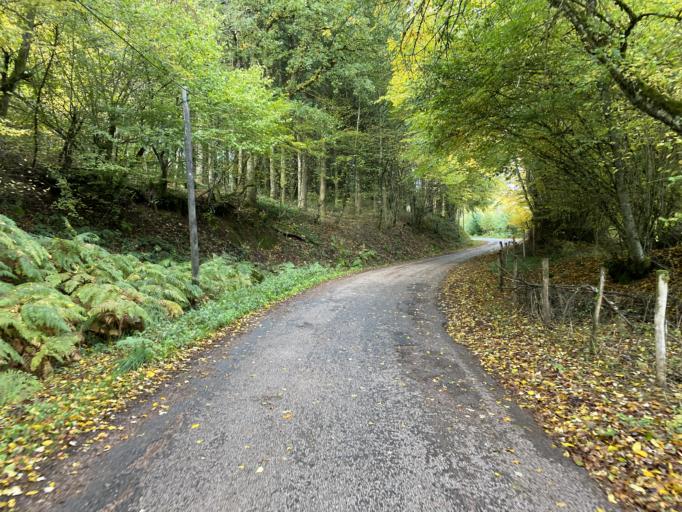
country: FR
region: Bourgogne
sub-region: Departement de la Cote-d'Or
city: Saulieu
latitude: 47.2612
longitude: 4.1727
